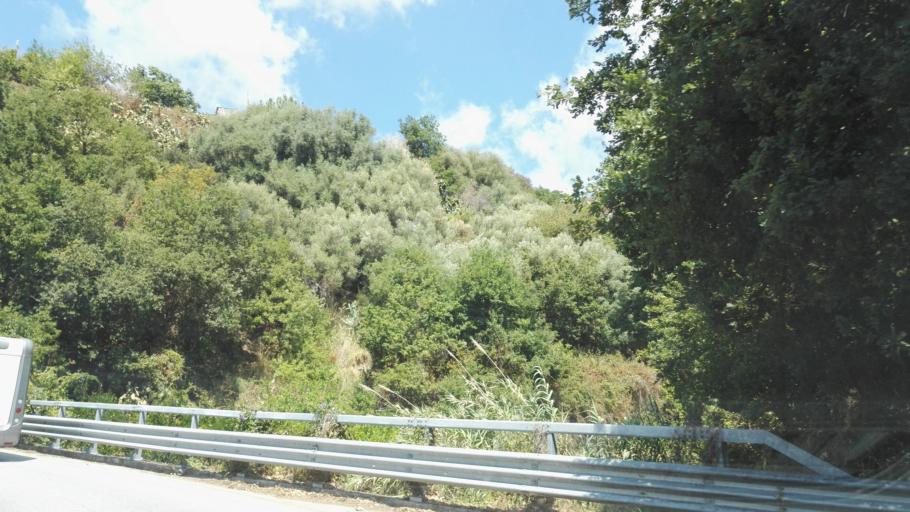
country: IT
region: Calabria
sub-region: Provincia di Vibo-Valentia
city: Joppolo
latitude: 38.5829
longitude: 15.8996
